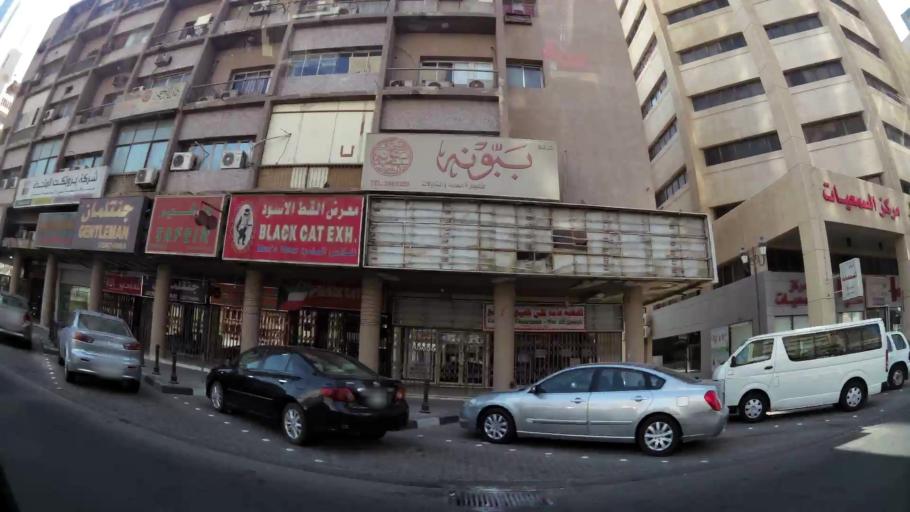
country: KW
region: Al Asimah
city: Kuwait City
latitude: 29.3678
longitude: 47.9682
